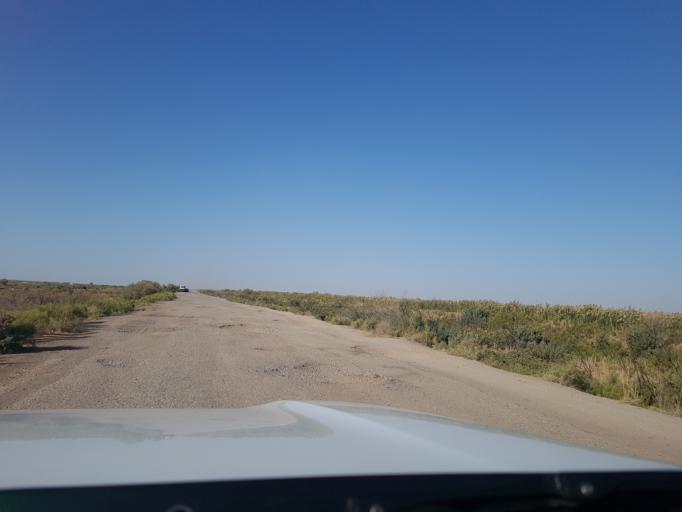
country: IR
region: Razavi Khorasan
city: Sarakhs
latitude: 36.9536
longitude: 61.3806
